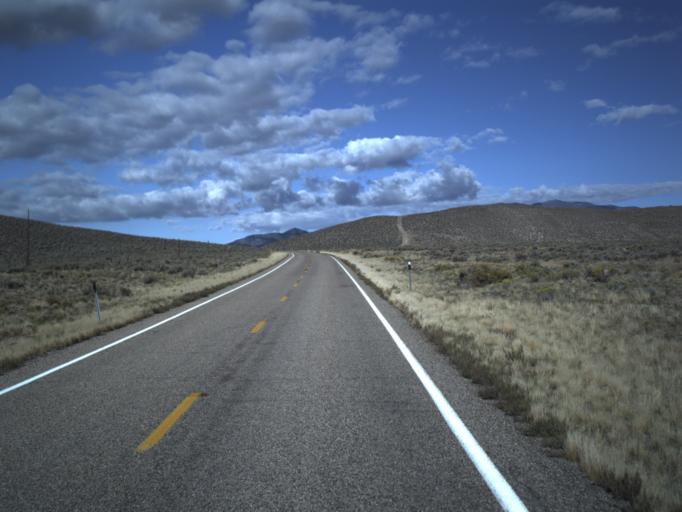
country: US
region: Utah
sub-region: Beaver County
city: Milford
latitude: 38.4224
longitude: -113.1050
